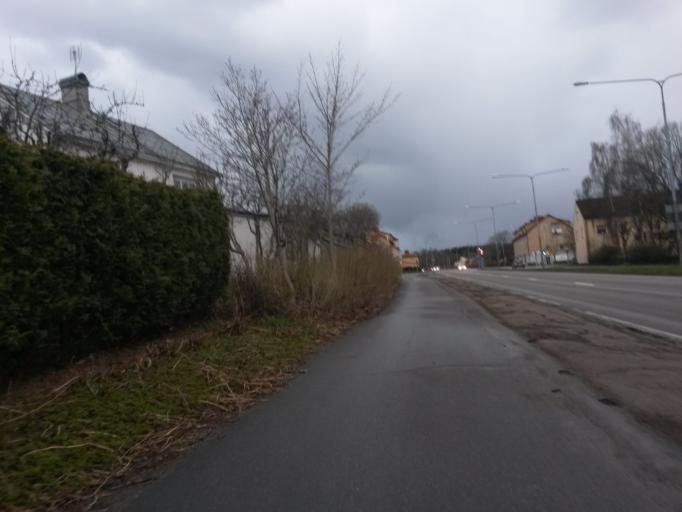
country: SE
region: OErebro
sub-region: Karlskoga Kommun
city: Karlskoga
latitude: 59.3209
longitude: 14.5050
